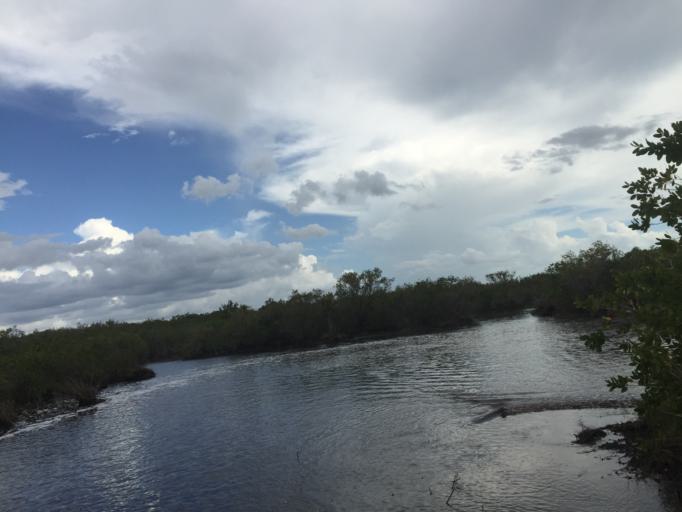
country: US
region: Florida
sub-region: Collier County
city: Marco
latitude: 25.8996
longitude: -81.3732
